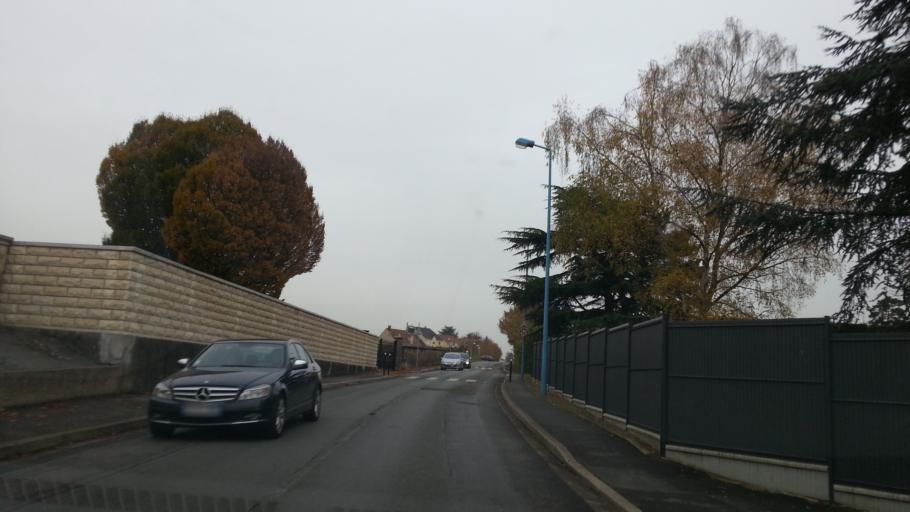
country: FR
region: Picardie
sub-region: Departement de l'Oise
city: Chambly
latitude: 49.1676
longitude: 2.2544
